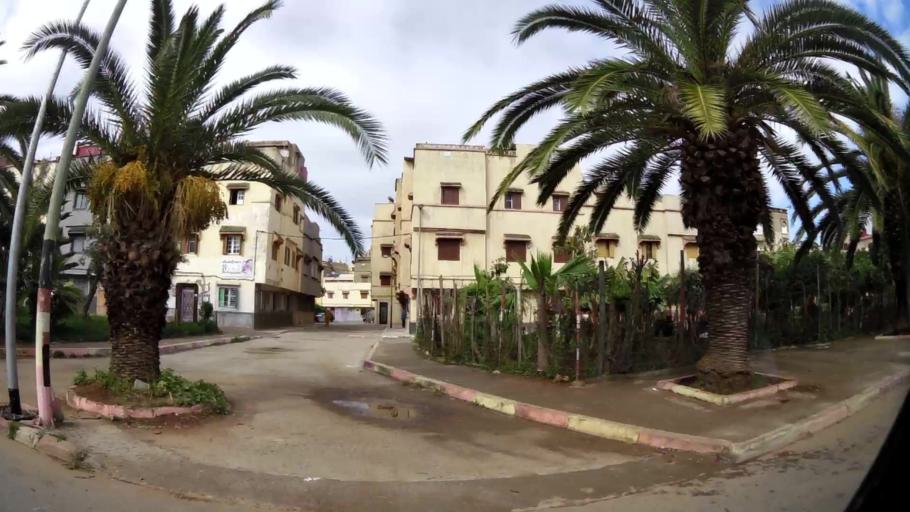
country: MA
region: Grand Casablanca
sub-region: Mohammedia
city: Mohammedia
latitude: 33.6845
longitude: -7.3761
